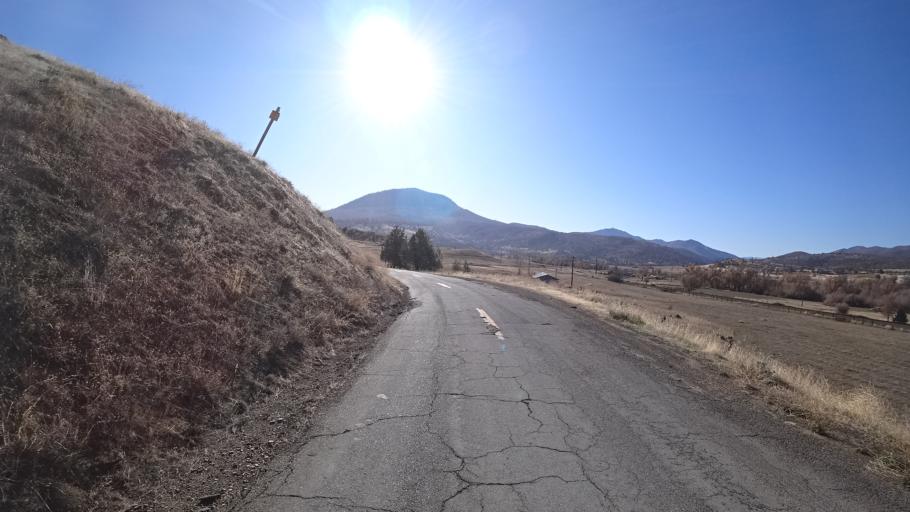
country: US
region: California
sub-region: Siskiyou County
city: Montague
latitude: 41.9029
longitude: -122.5467
